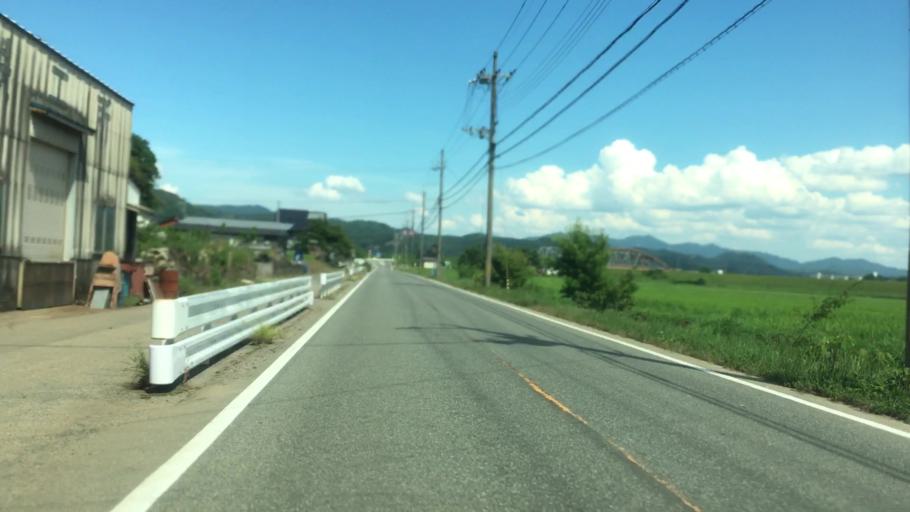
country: JP
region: Hyogo
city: Toyooka
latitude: 35.5663
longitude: 134.7986
